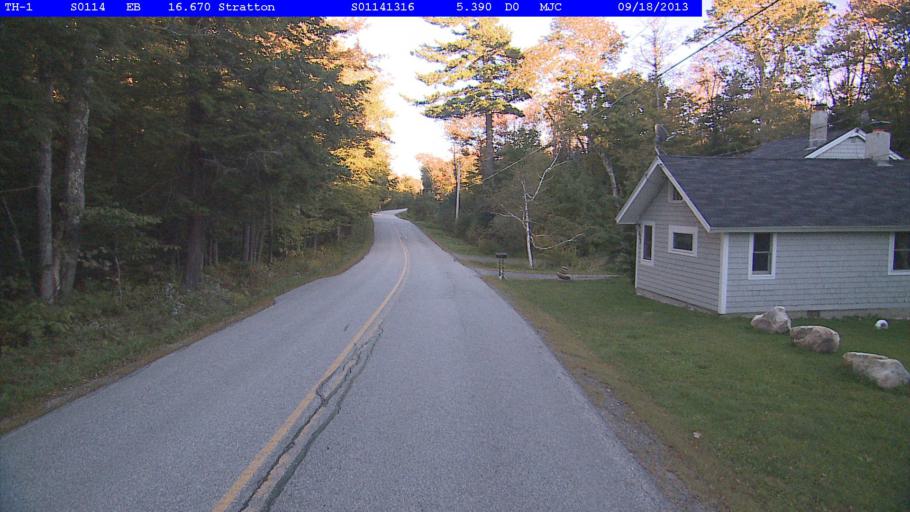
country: US
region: Vermont
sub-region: Windham County
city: Dover
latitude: 43.0414
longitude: -72.9077
